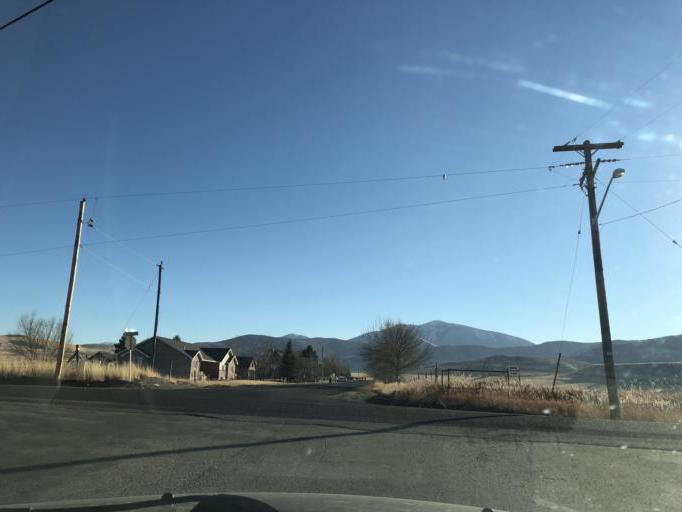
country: US
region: Utah
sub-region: Cache County
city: Wellsville
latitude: 41.6075
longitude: -111.9299
